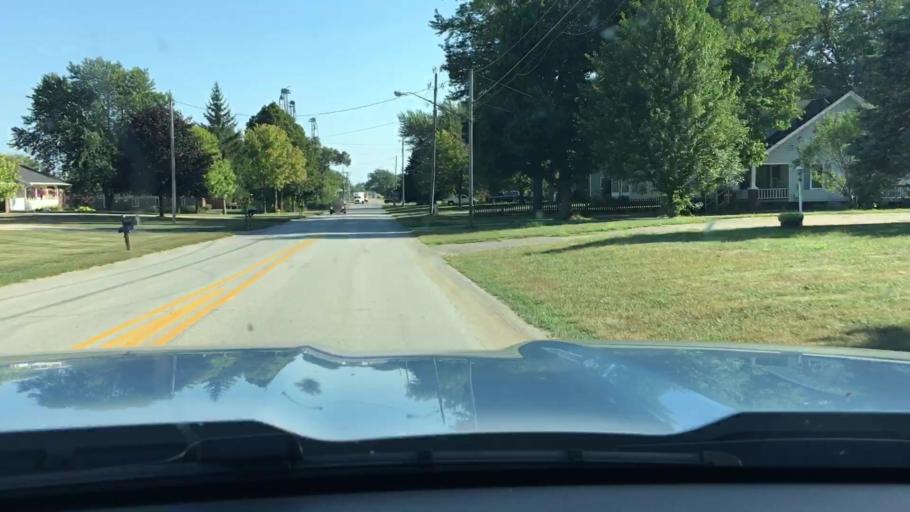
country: US
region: Michigan
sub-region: Ottawa County
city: Zeeland
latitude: 42.8143
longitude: -85.9401
